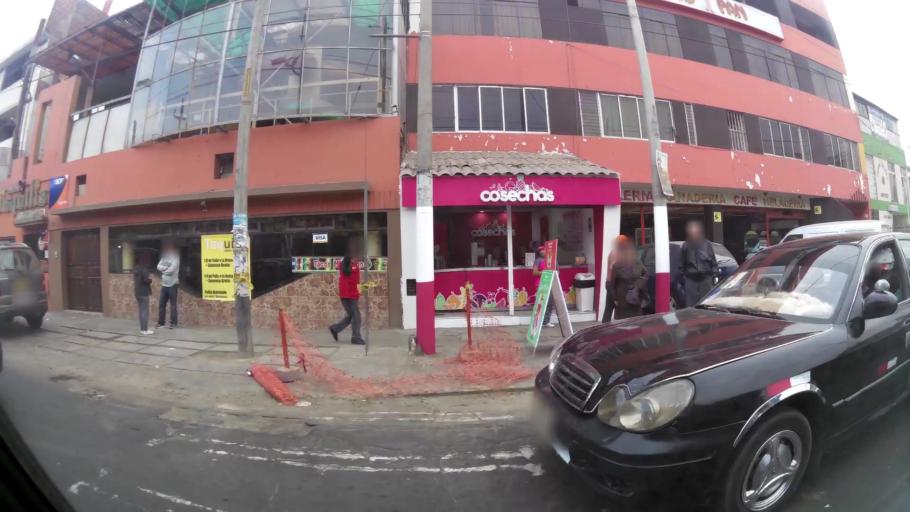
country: PE
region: La Libertad
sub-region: Provincia de Trujillo
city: Trujillo
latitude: -8.1036
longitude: -79.0320
